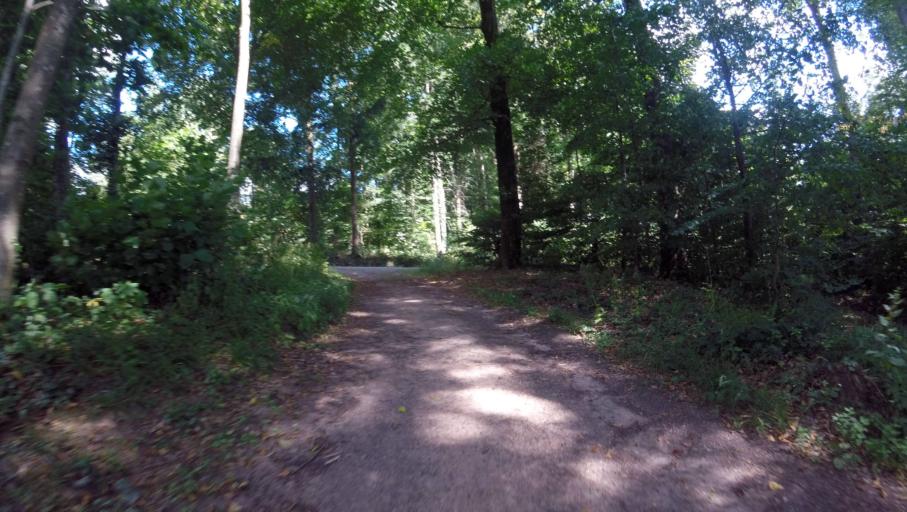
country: DE
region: Baden-Wuerttemberg
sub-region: Regierungsbezirk Stuttgart
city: Oppenweiler
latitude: 49.0072
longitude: 9.4628
